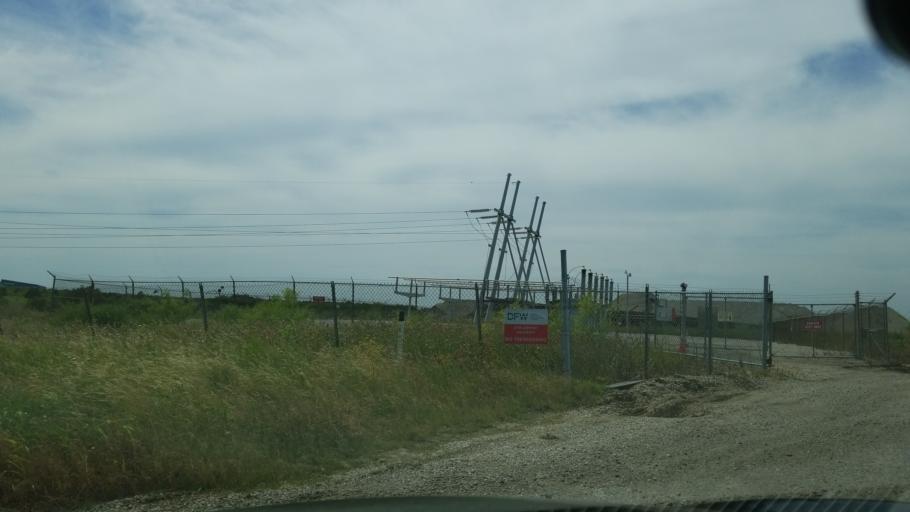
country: US
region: Texas
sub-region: Dallas County
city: Coppell
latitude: 32.8875
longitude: -96.9983
